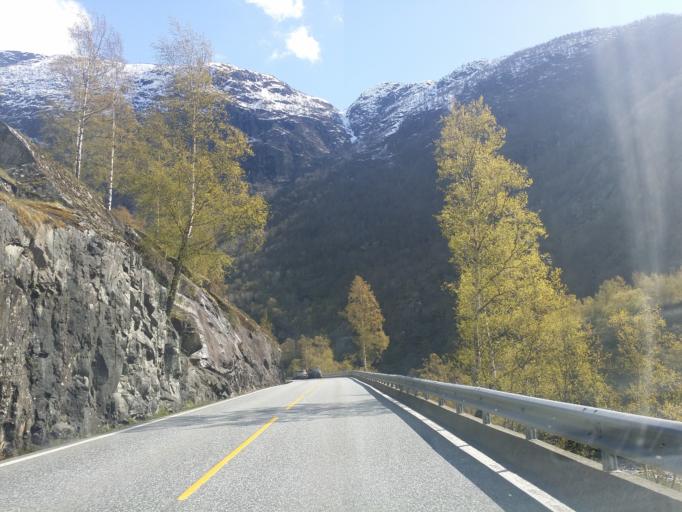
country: NO
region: Hordaland
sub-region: Eidfjord
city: Eidfjord
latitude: 60.4200
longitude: 7.1417
